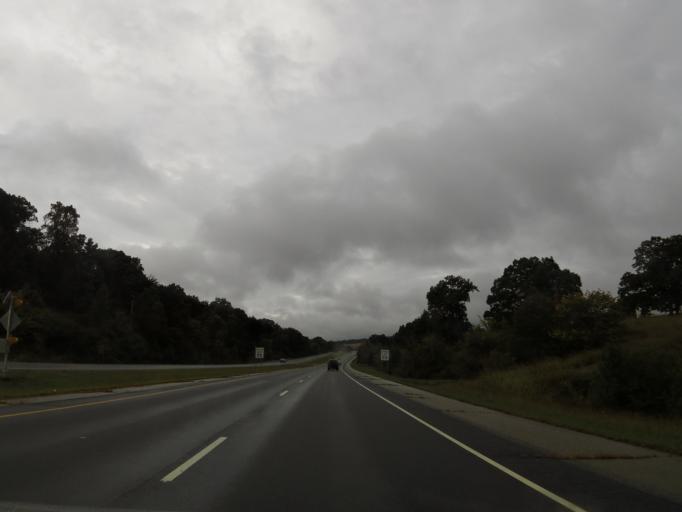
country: US
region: Tennessee
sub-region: Blount County
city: Louisville
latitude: 35.7570
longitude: -84.0497
